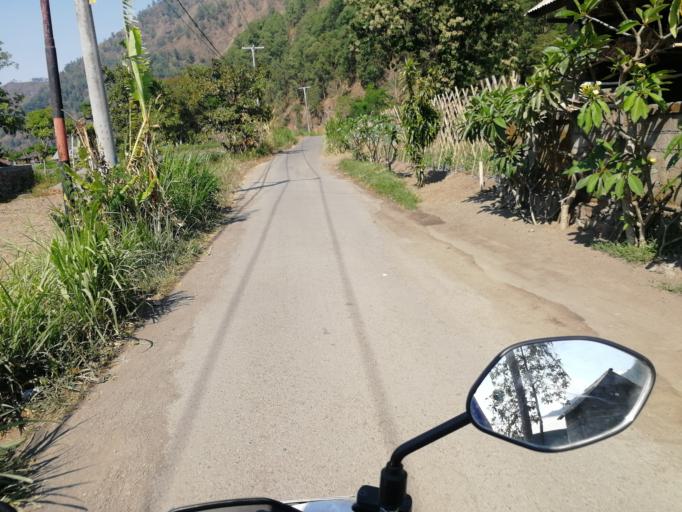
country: ID
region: Bali
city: Banjar Trunyan
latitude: -8.2709
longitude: 115.4159
